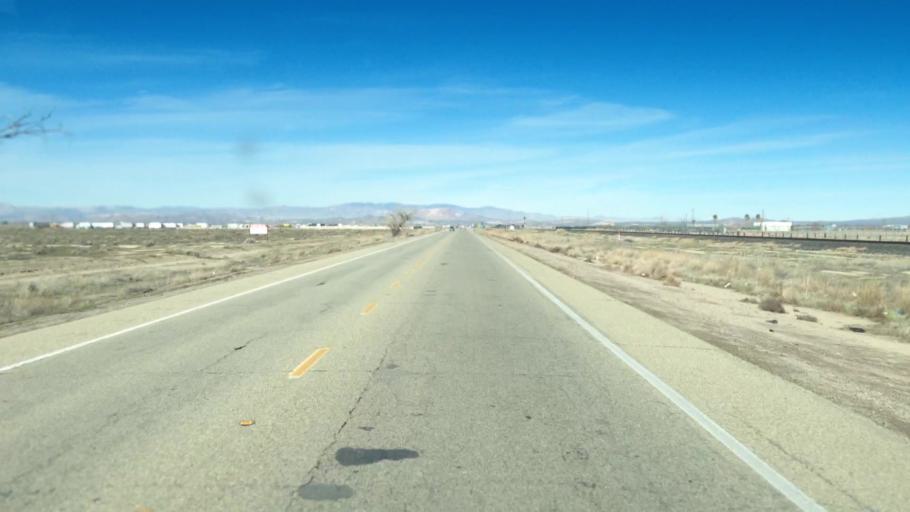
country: US
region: California
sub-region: Los Angeles County
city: Lancaster
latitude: 34.7285
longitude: -118.1414
